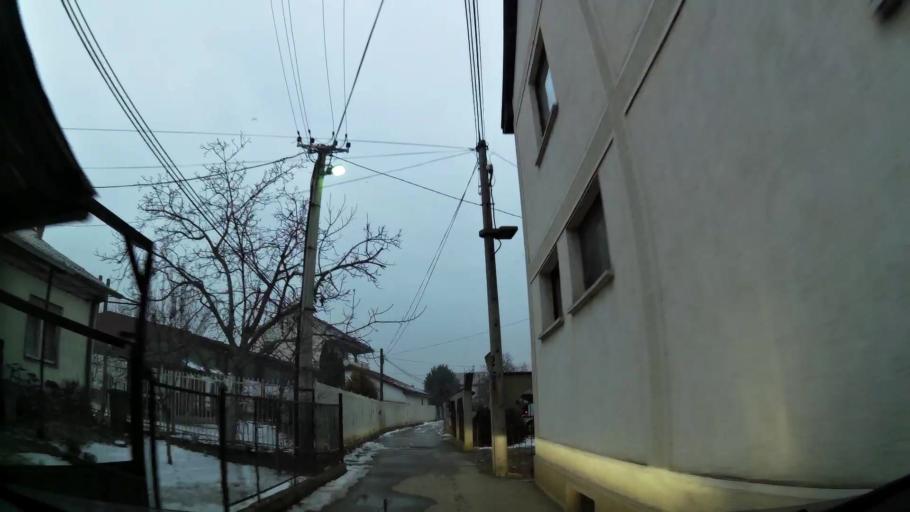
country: MK
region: Kisela Voda
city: Usje
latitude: 41.9751
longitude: 21.4828
